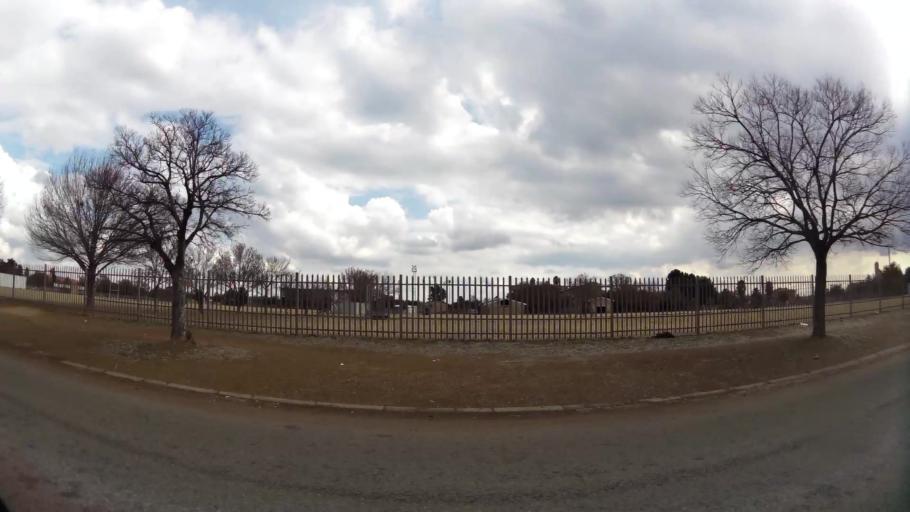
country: ZA
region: Gauteng
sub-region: Sedibeng District Municipality
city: Vanderbijlpark
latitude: -26.7235
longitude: 27.8489
